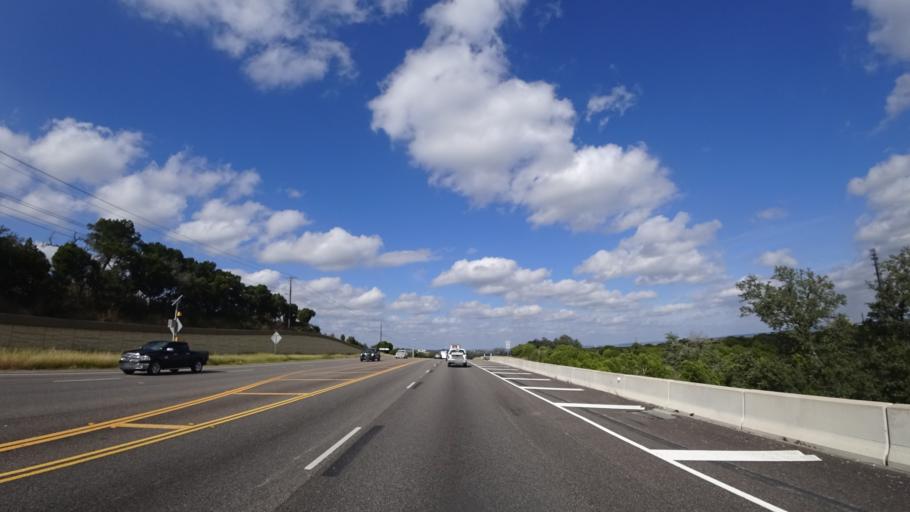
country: US
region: Texas
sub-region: Travis County
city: Bee Cave
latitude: 30.2786
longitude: -97.9159
